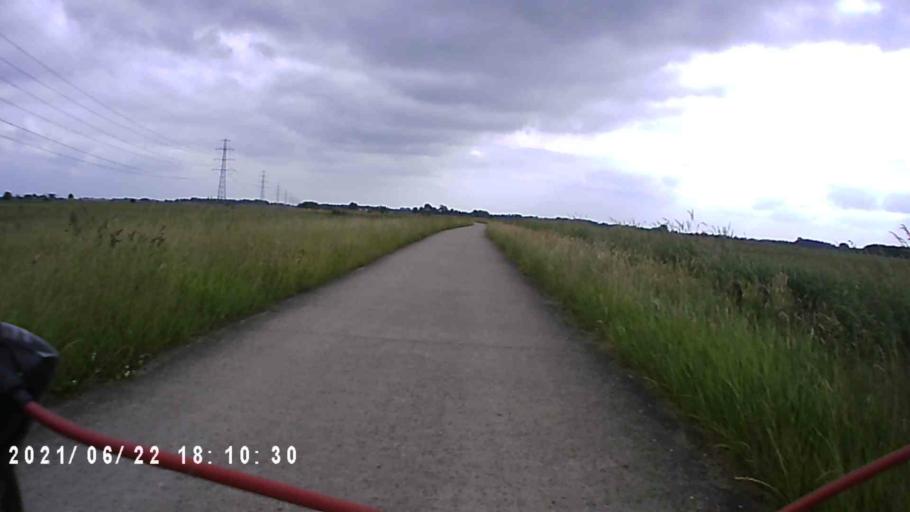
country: NL
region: Groningen
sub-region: Gemeente Groningen
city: Groningen
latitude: 53.1834
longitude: 6.4952
